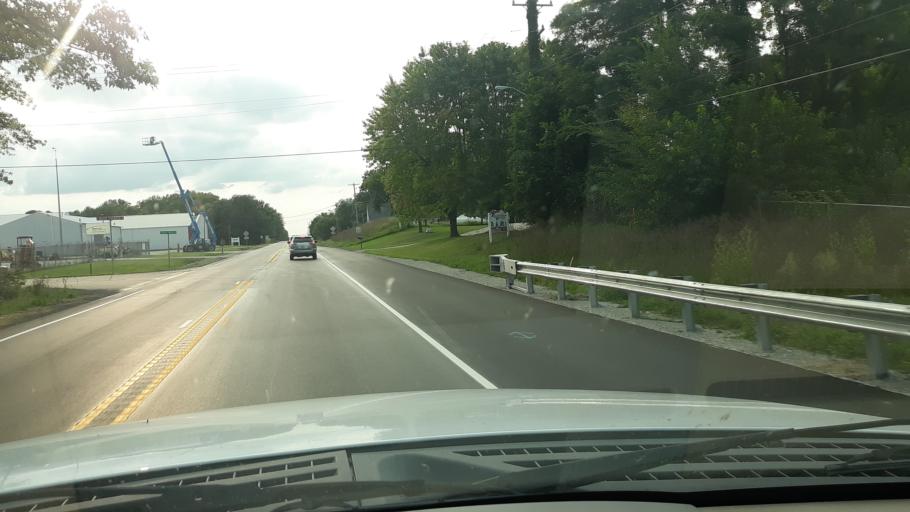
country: US
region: Indiana
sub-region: Gibson County
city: Princeton
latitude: 38.3556
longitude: -87.6118
